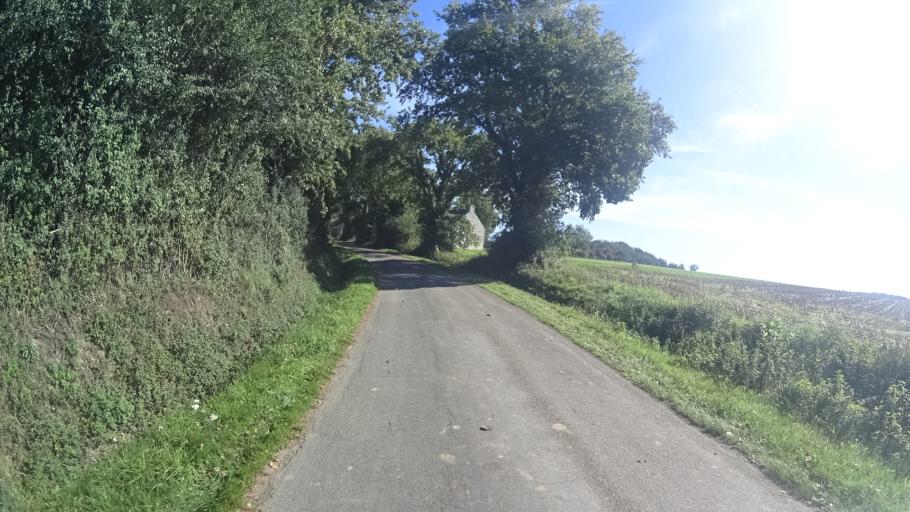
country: FR
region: Brittany
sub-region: Departement du Morbihan
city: Peillac
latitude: 47.7378
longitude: -2.1920
